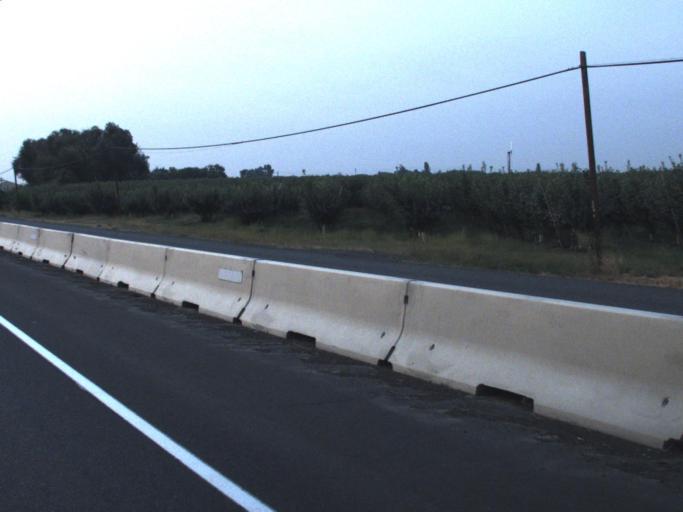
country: US
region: Washington
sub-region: Yakima County
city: Wapato
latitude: 46.4674
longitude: -120.4391
